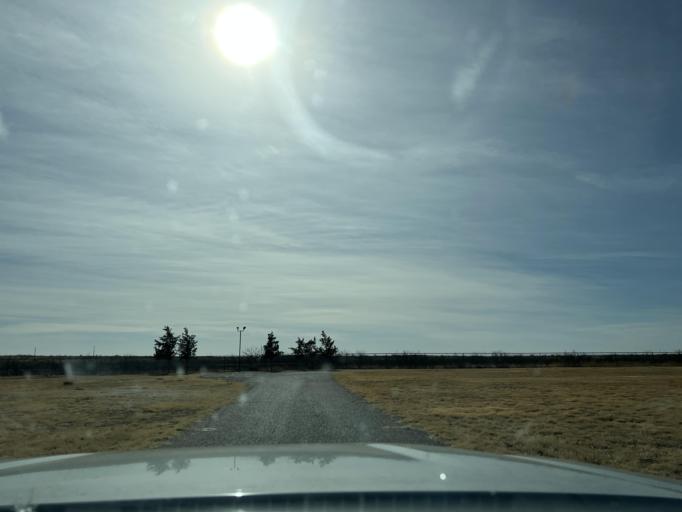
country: US
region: Texas
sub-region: Andrews County
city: Andrews
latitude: 32.4529
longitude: -102.5706
